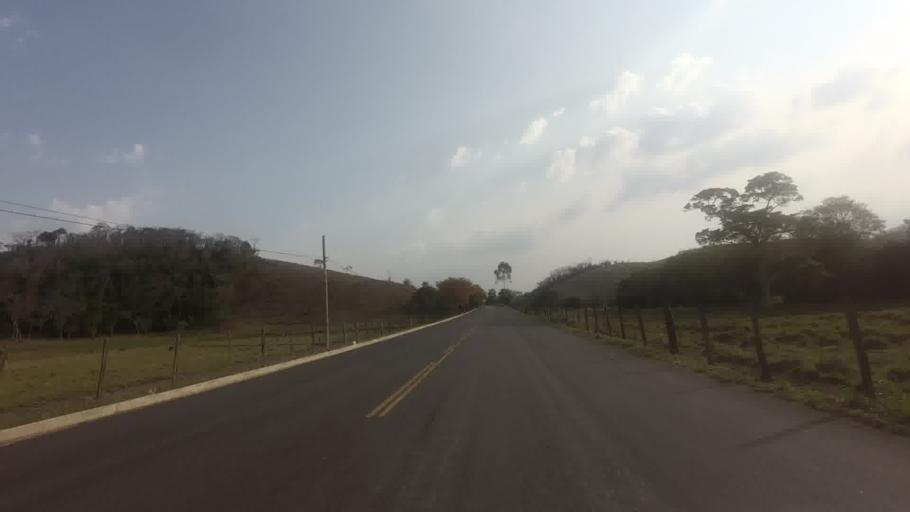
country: BR
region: Rio de Janeiro
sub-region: Cambuci
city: Cambuci
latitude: -21.3935
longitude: -41.9724
